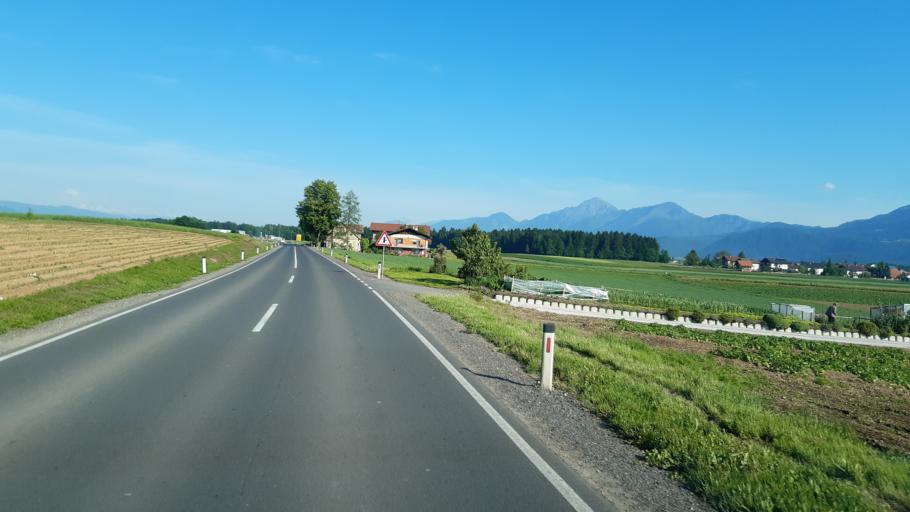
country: SI
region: Komenda
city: Komenda
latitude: 46.1997
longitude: 14.5372
